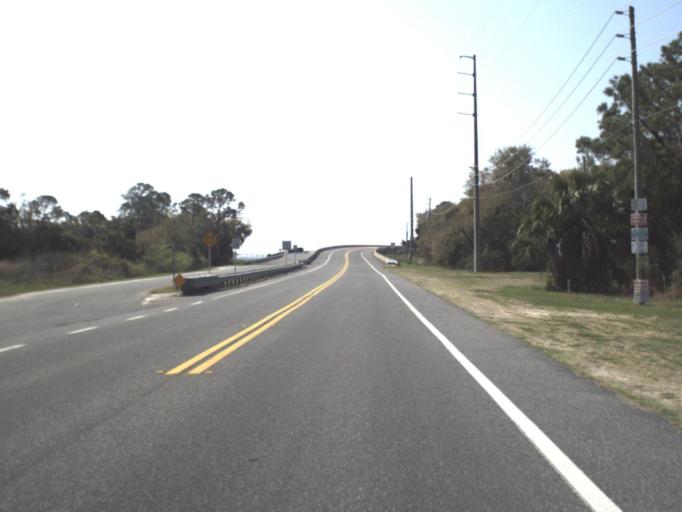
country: US
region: Florida
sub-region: Franklin County
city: Eastpoint
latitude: 29.7262
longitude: -84.8880
